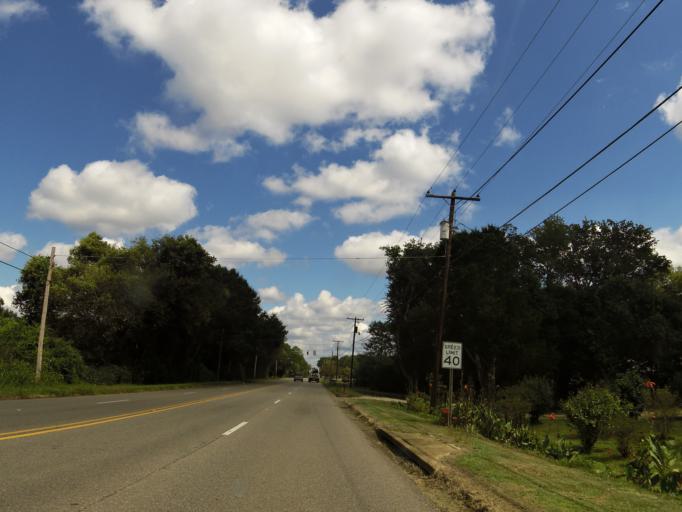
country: US
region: Alabama
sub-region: Dallas County
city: Selma
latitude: 32.3886
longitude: -87.0801
